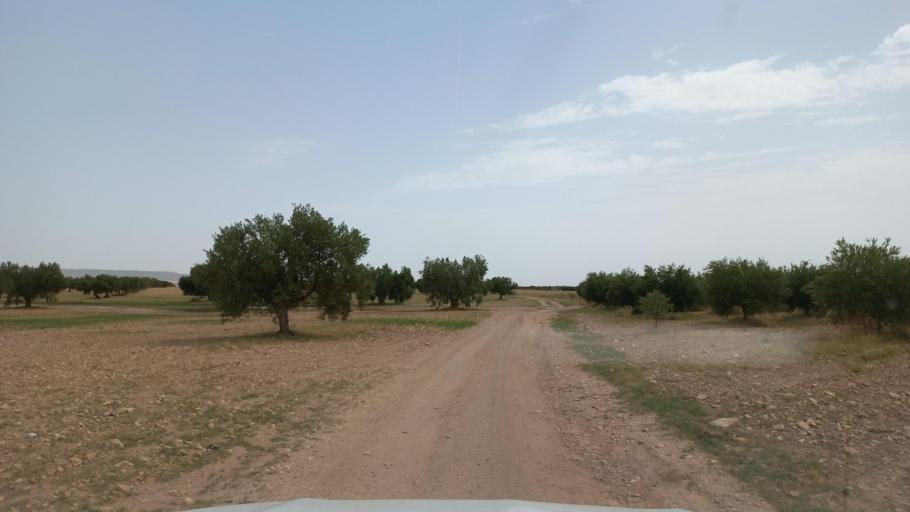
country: TN
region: Al Qasrayn
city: Kasserine
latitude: 35.2890
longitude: 9.0270
